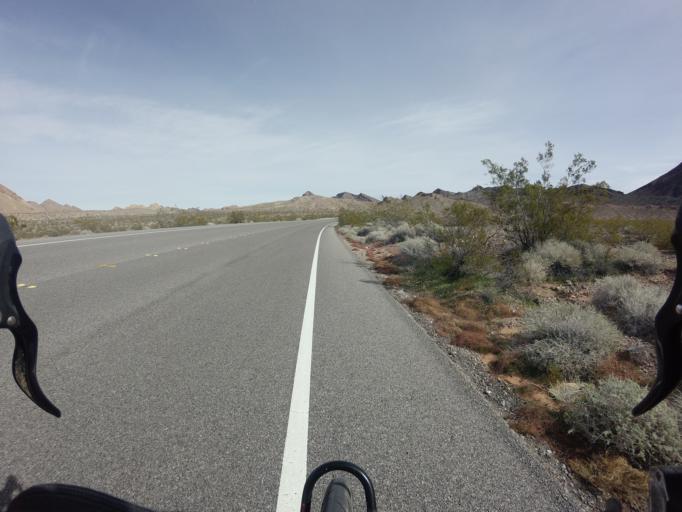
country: US
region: Nevada
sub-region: Clark County
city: Boulder City
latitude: 36.2009
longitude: -114.6744
